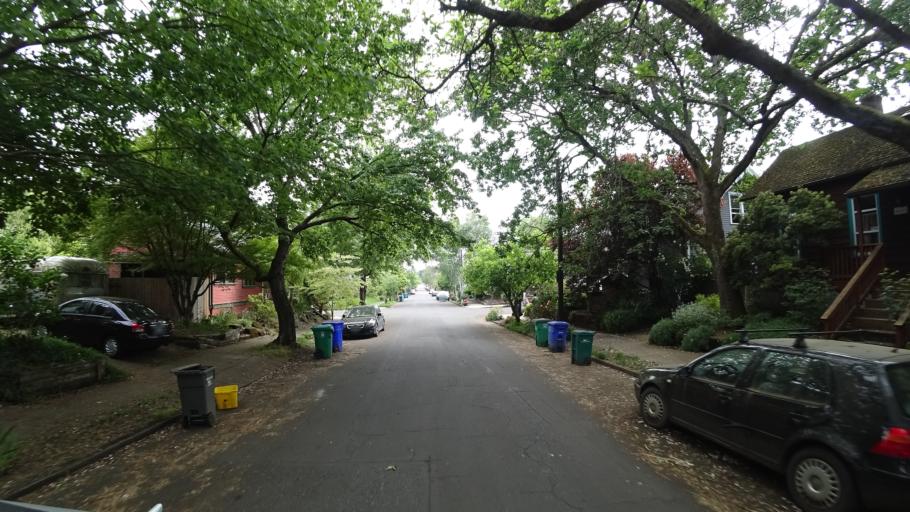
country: US
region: Oregon
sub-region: Multnomah County
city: Portland
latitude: 45.5524
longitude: -122.6527
